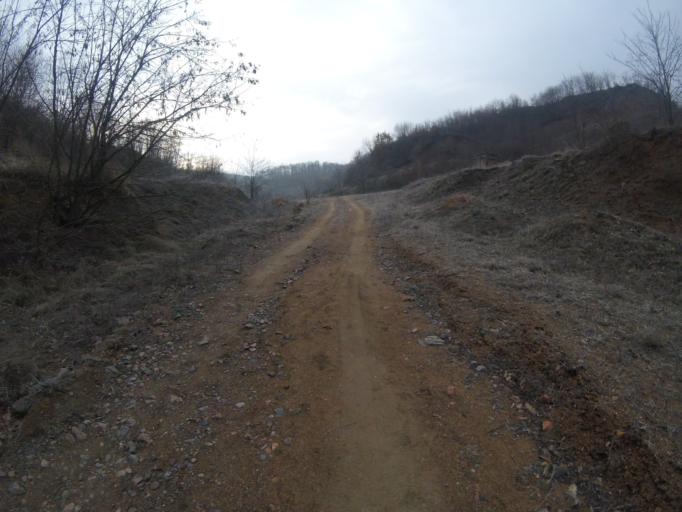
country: HU
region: Baranya
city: Mecseknadasd
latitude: 46.1494
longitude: 18.5183
